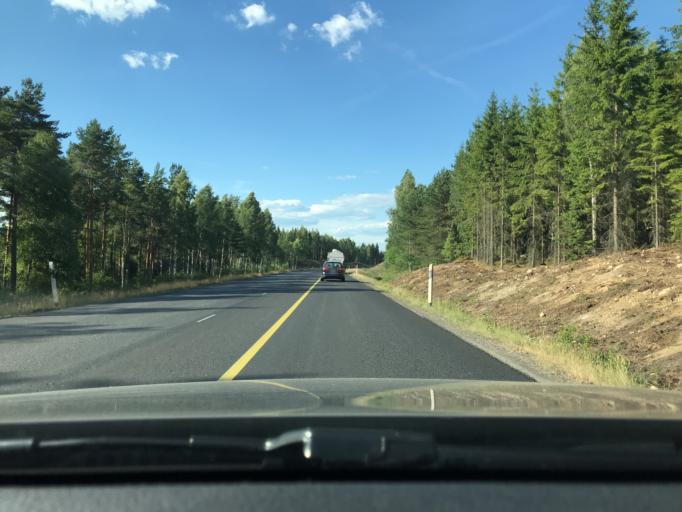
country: SE
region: Kronoberg
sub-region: Almhults Kommun
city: AElmhult
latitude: 56.5710
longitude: 14.1842
